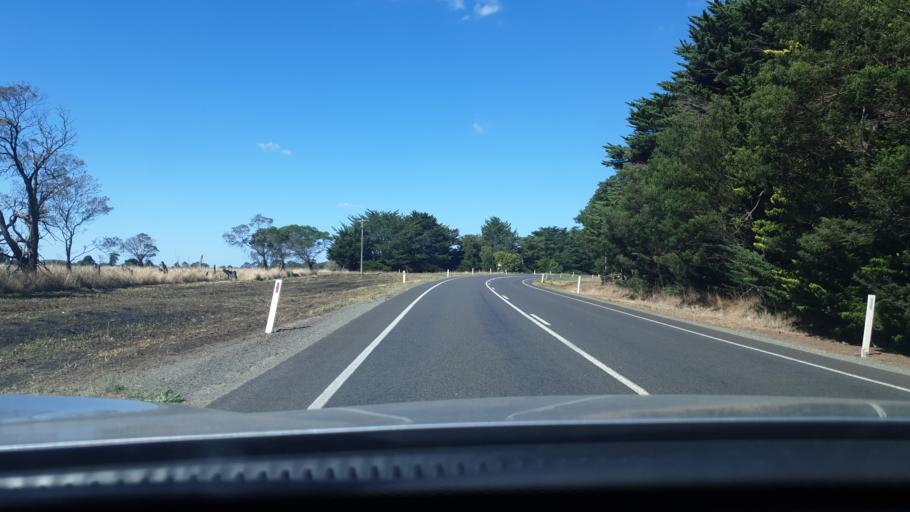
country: AU
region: Victoria
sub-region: Warrnambool
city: Warrnambool
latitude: -38.1780
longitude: 142.4212
